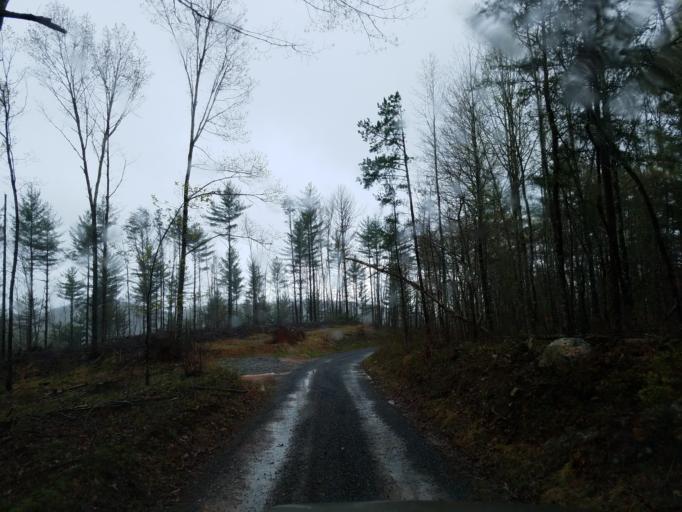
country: US
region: Georgia
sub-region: Fannin County
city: Blue Ridge
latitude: 34.8385
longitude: -84.2348
